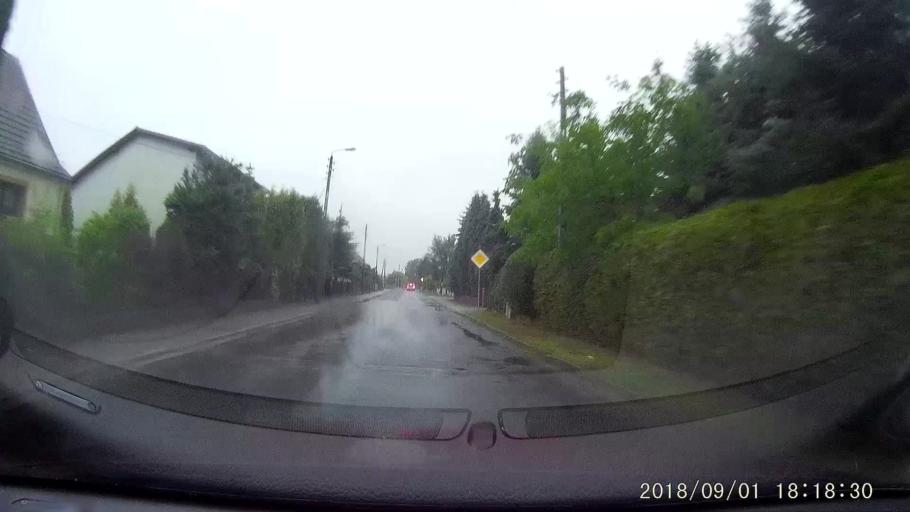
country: PL
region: Lower Silesian Voivodeship
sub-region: Powiat zgorzelecki
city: Piensk
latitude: 51.2592
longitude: 15.0457
